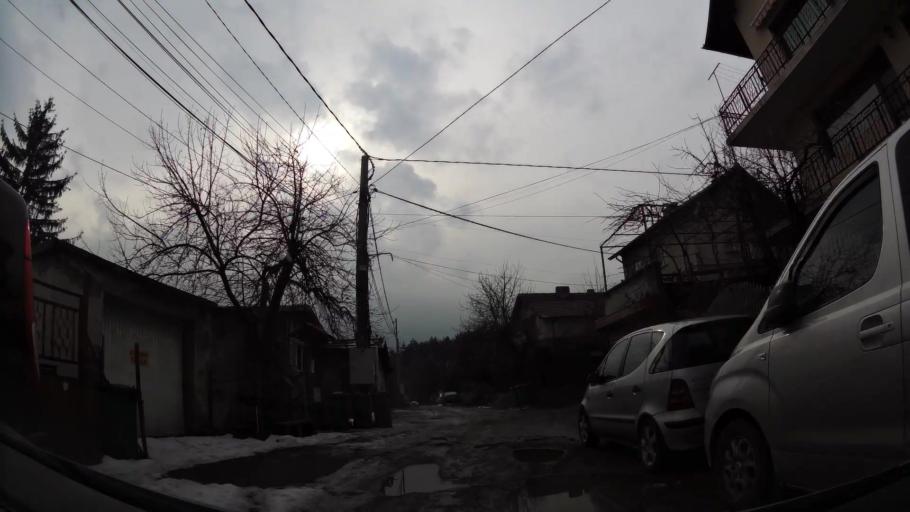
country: BG
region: Sofia-Capital
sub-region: Stolichna Obshtina
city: Sofia
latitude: 42.6607
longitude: 23.2382
